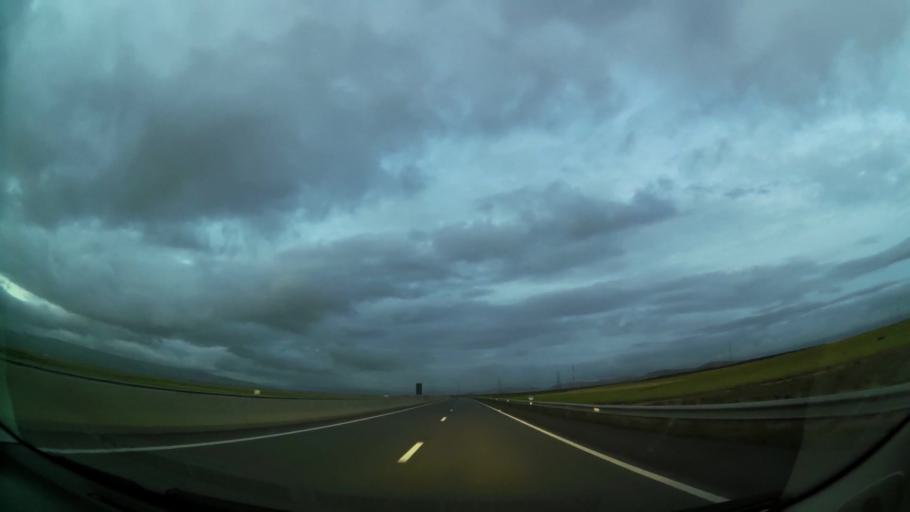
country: MA
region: Oriental
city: El Aioun
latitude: 34.6322
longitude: -2.3353
